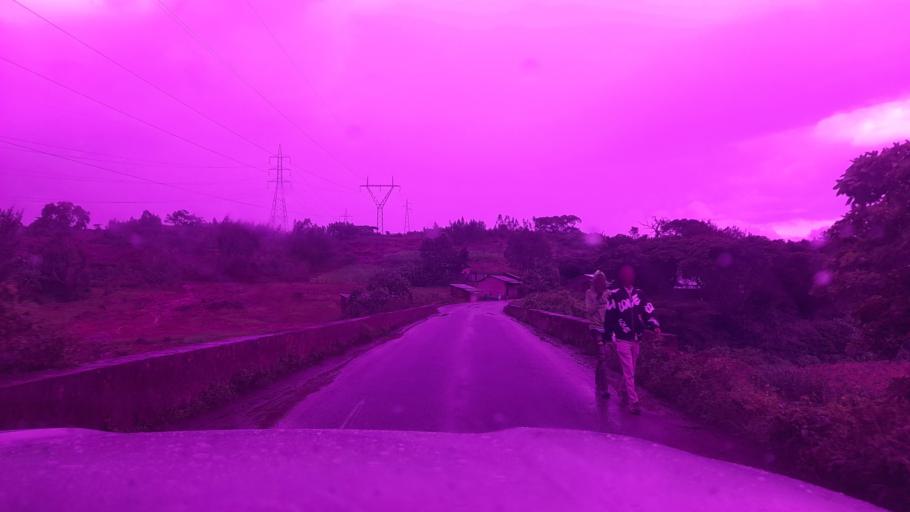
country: ET
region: Oromiya
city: Jima
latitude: 7.7145
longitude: 37.0865
